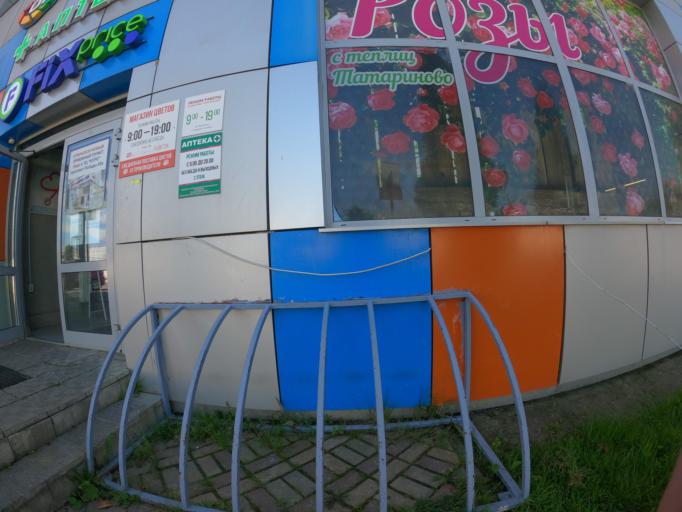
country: RU
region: Moskovskaya
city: Stupino
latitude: 54.8968
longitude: 38.0750
